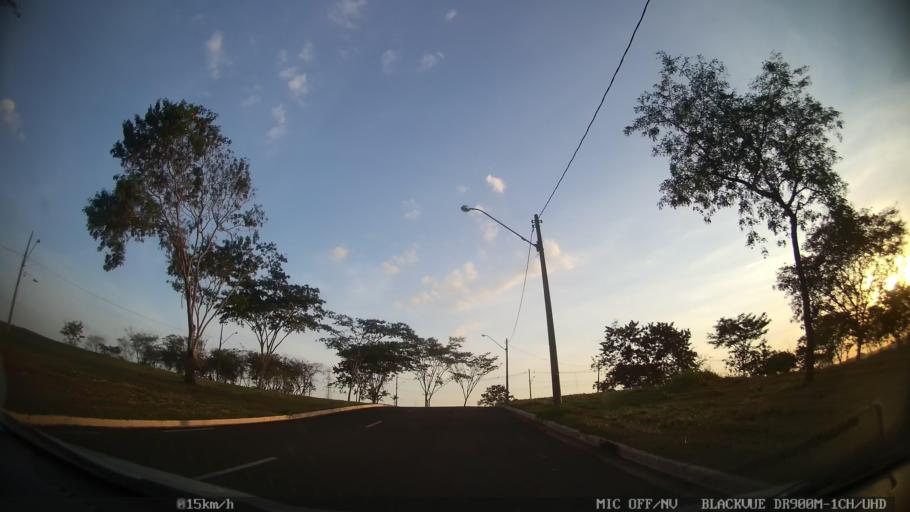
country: BR
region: Sao Paulo
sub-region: Ribeirao Preto
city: Ribeirao Preto
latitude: -21.1417
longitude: -47.8562
